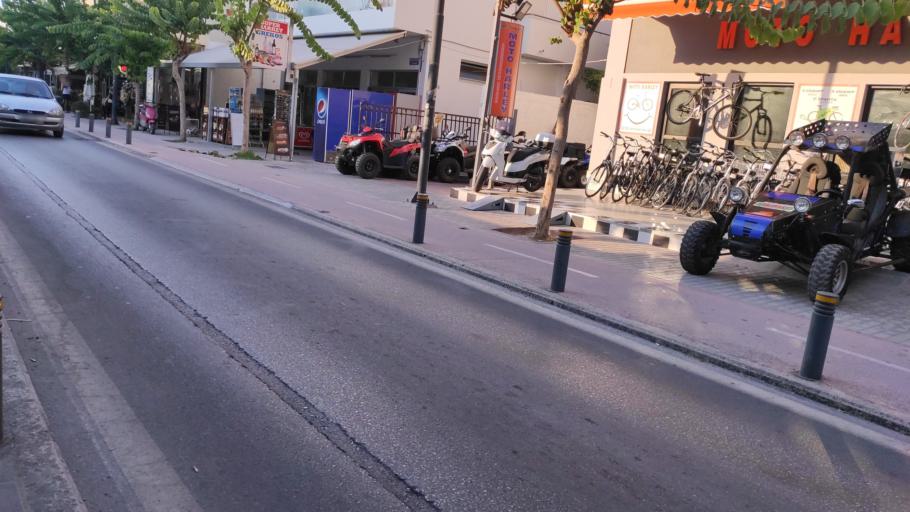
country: GR
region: South Aegean
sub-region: Nomos Dodekanisou
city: Kos
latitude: 36.8995
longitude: 27.2837
